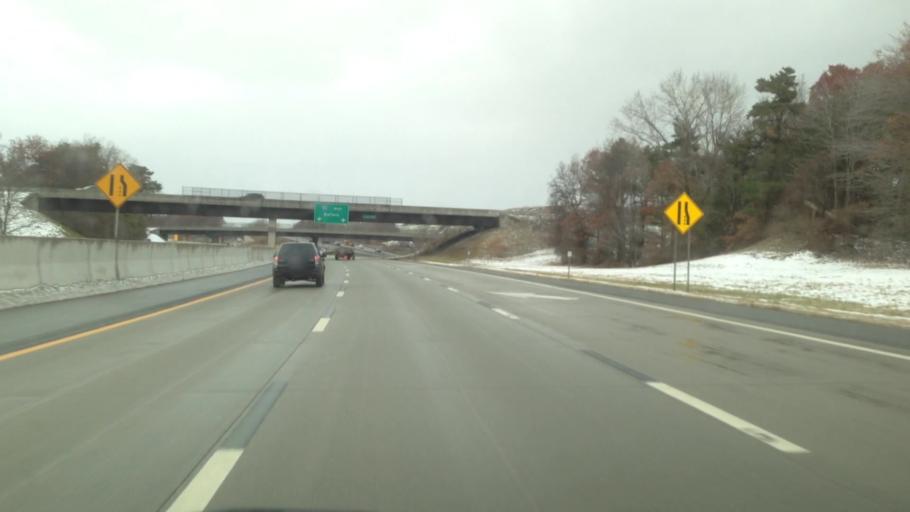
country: US
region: New York
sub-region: Albany County
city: McKownville
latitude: 42.7004
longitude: -73.8475
